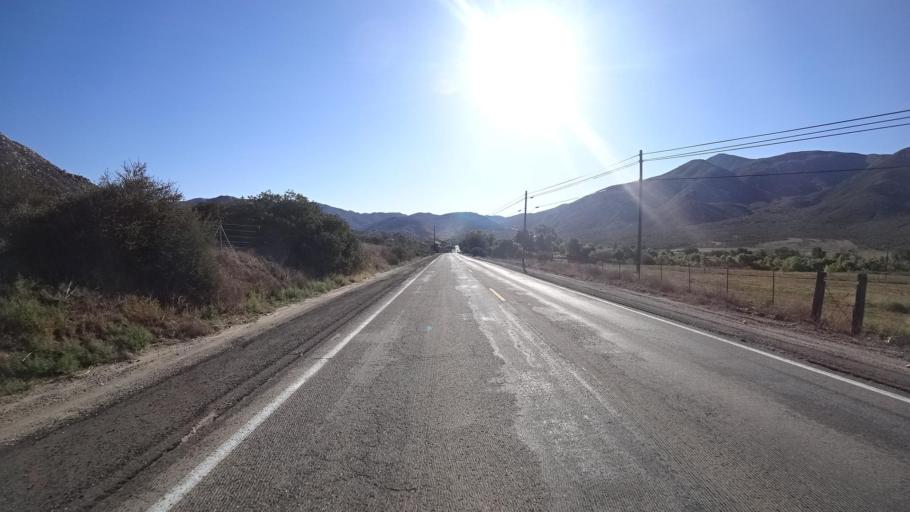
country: MX
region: Baja California
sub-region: Tecate
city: Lomas de Santa Anita
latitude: 32.6133
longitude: -116.7118
